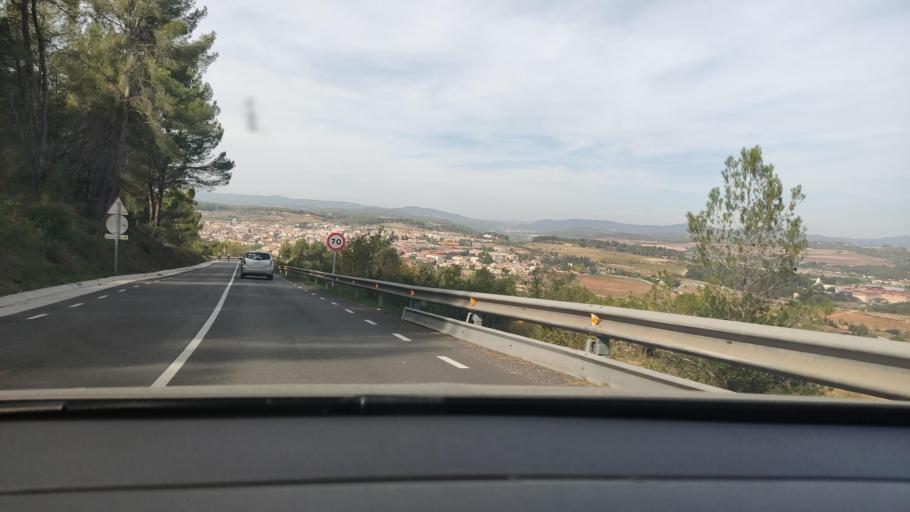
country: ES
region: Catalonia
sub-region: Provincia de Barcelona
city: Sant Sadurni d'Anoia
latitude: 41.4163
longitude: 1.8030
